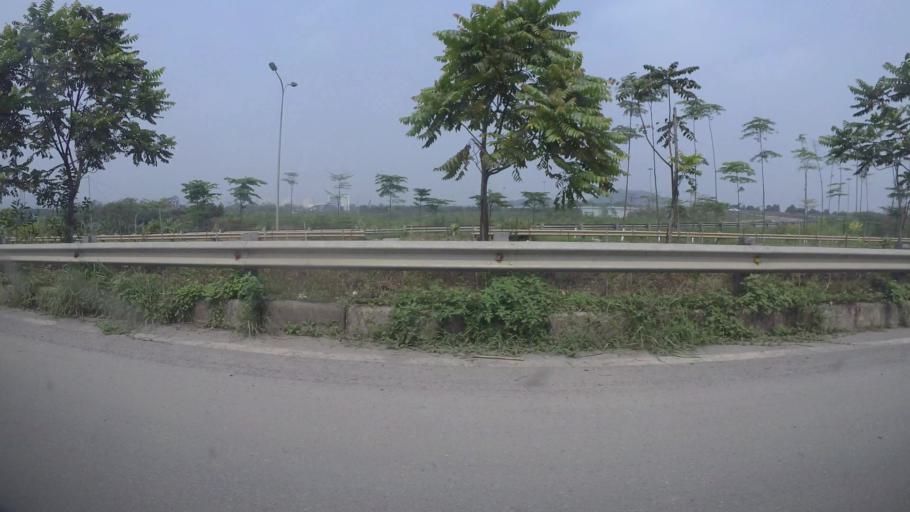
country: VN
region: Ha Noi
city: Lien Quan
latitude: 20.9889
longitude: 105.5286
